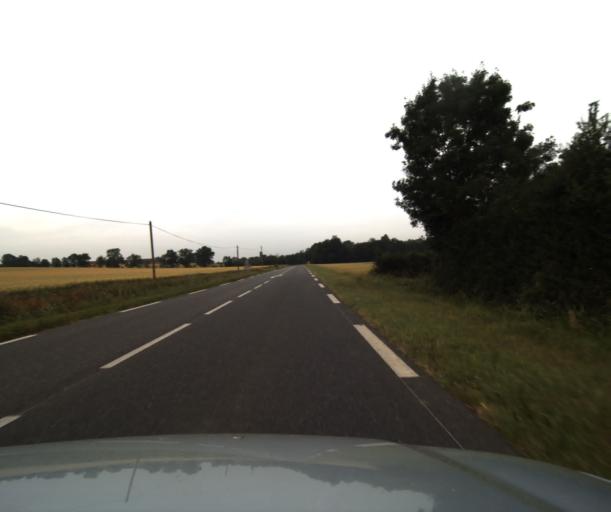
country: FR
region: Midi-Pyrenees
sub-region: Departement du Gers
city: Gimont
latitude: 43.7098
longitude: 0.8578
